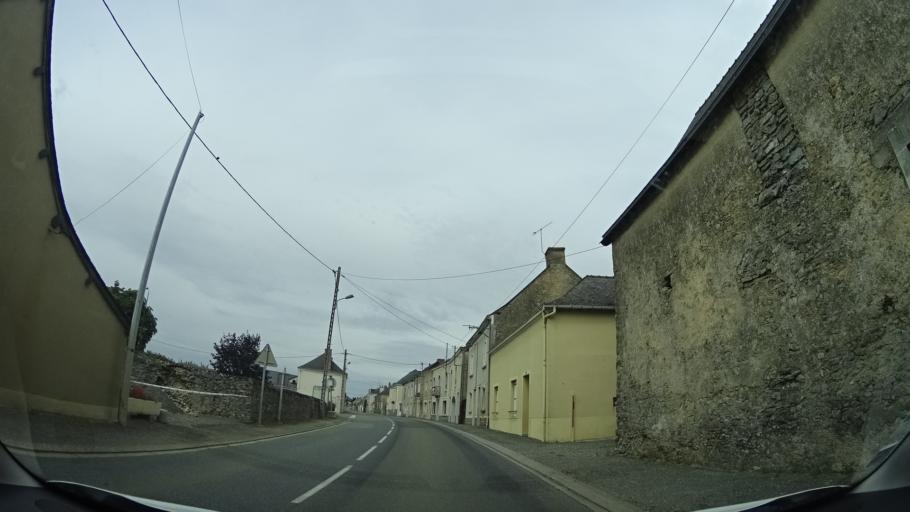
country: FR
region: Pays de la Loire
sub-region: Departement de la Sarthe
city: Auvers-le-Hamon
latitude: 47.8900
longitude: -0.4162
